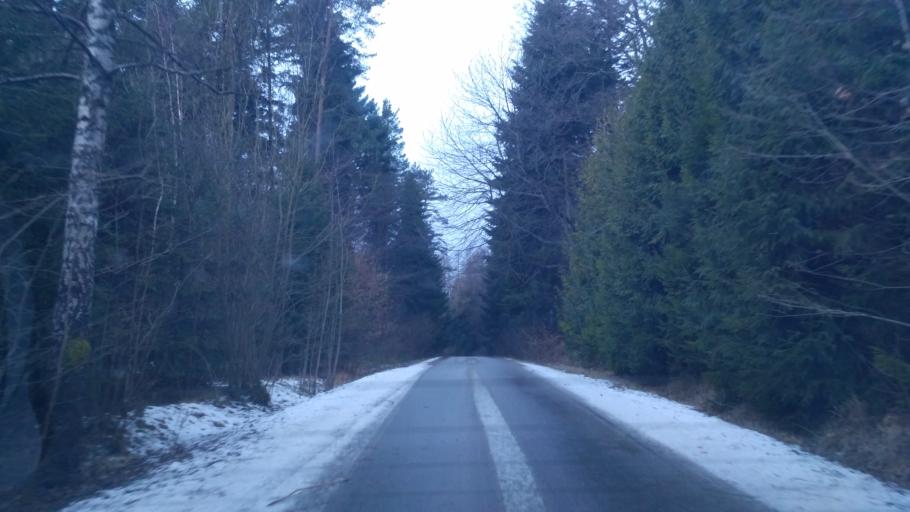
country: PL
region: Subcarpathian Voivodeship
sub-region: Powiat rzeszowski
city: Hyzne
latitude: 49.8964
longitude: 22.1610
